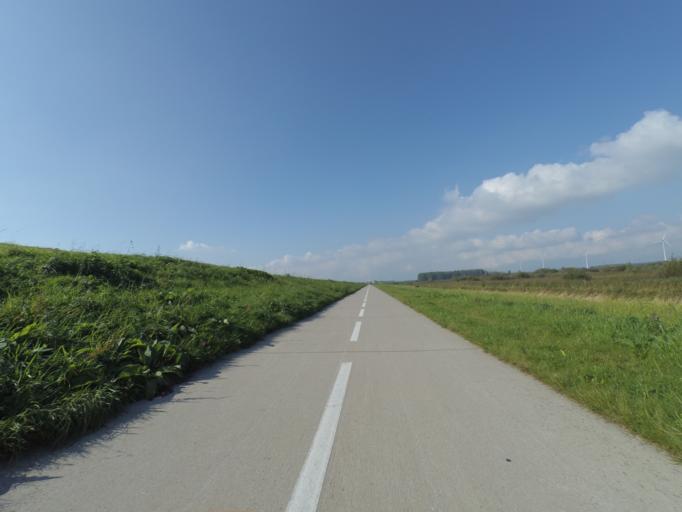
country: NL
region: Flevoland
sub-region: Gemeente Zeewolde
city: Zeewolde
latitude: 52.3652
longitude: 5.5743
